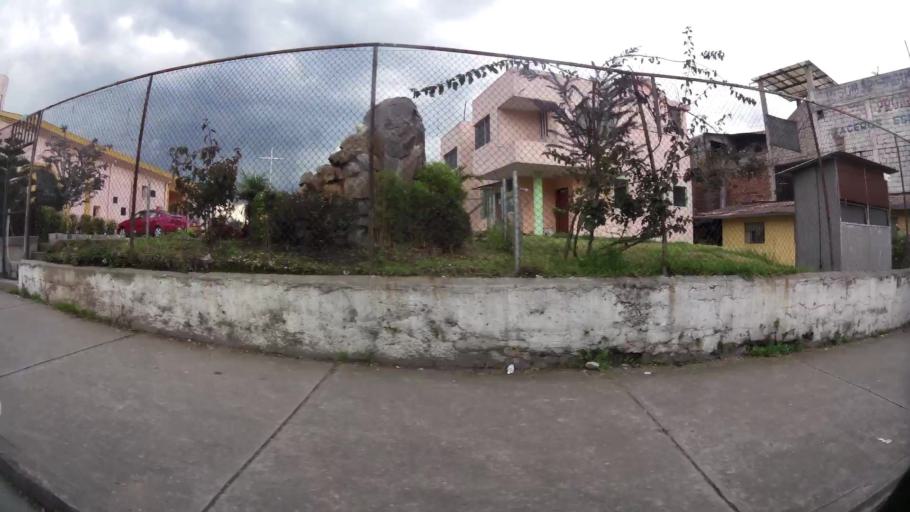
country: EC
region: Pichincha
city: Quito
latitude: -0.2745
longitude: -78.5367
